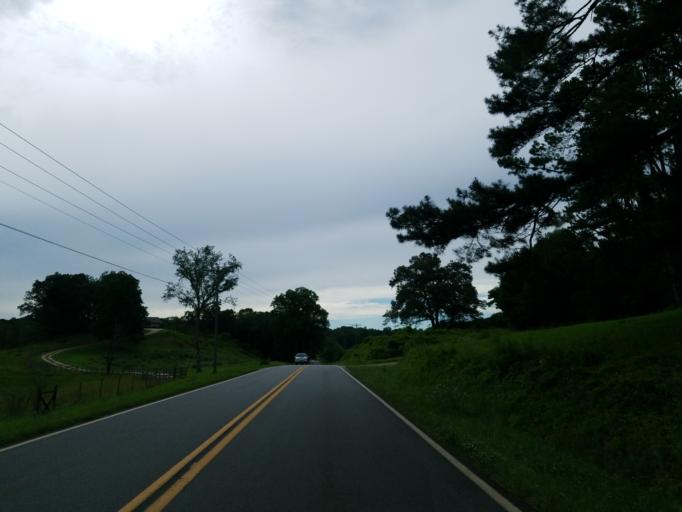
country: US
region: Georgia
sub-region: Lumpkin County
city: Dahlonega
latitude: 34.5638
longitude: -83.9529
